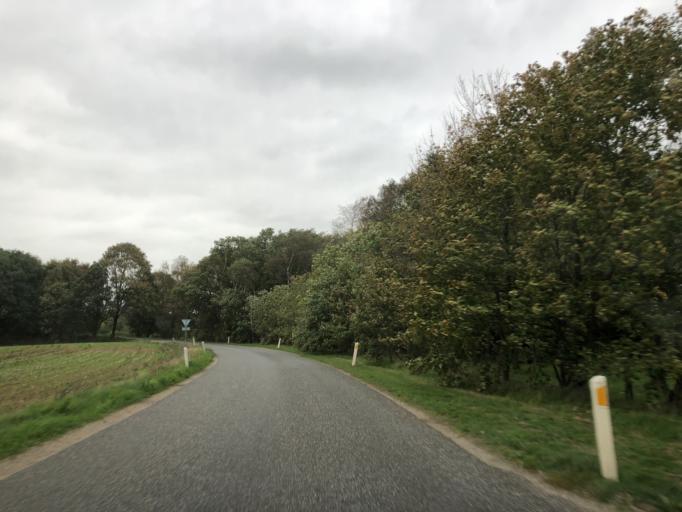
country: DK
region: Central Jutland
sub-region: Viborg Kommune
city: Viborg
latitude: 56.3874
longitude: 9.3052
